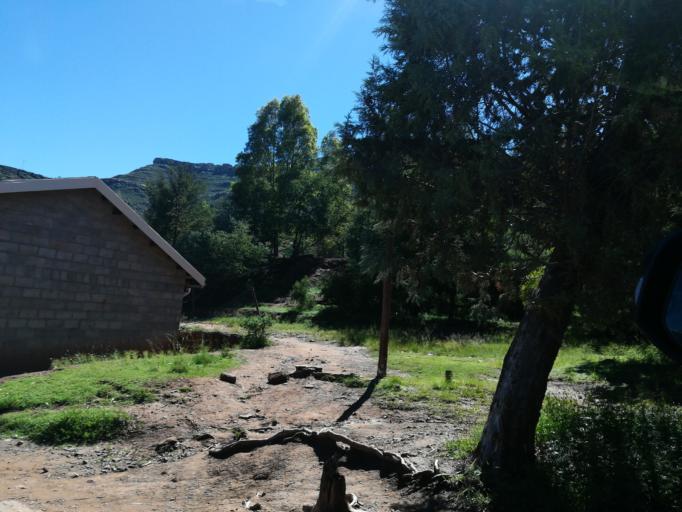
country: LS
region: Quthing
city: Quthing
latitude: -30.3414
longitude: 27.5451
